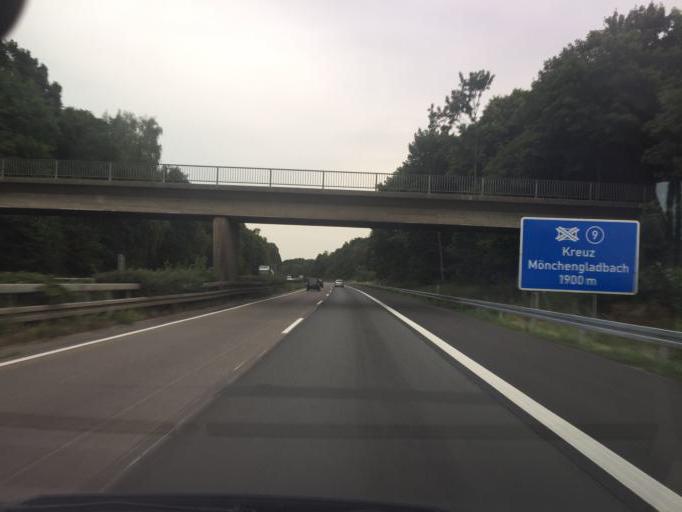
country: DE
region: North Rhine-Westphalia
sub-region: Regierungsbezirk Dusseldorf
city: Viersen
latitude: 51.2297
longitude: 6.3625
